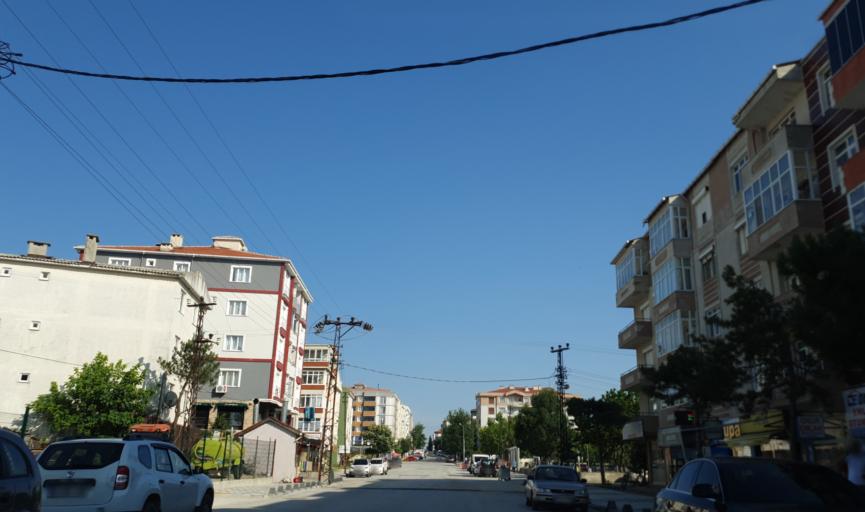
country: TR
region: Tekirdag
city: Saray
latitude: 41.4457
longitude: 27.9167
